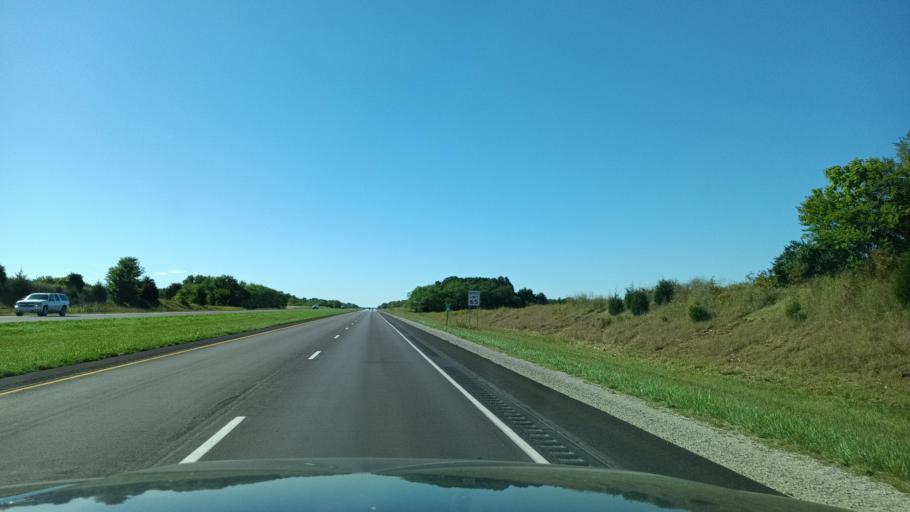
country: US
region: Illinois
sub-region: Hancock County
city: Nauvoo
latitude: 40.4913
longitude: -91.4439
